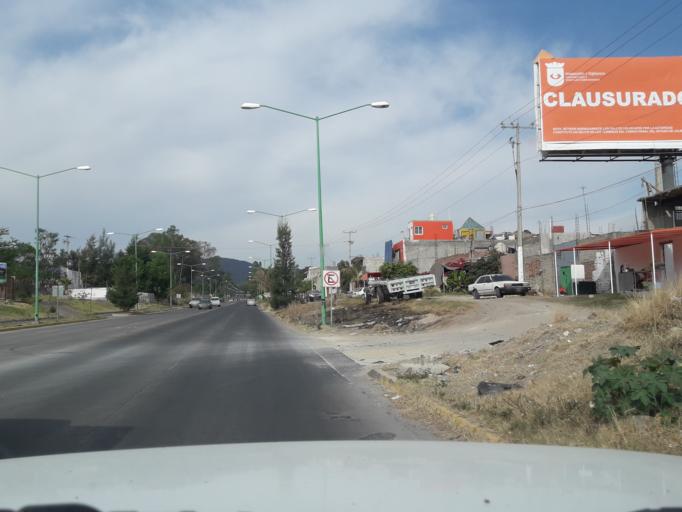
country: MX
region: Jalisco
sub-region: Tlajomulco de Zuniga
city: Palomar
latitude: 20.6216
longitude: -103.4740
